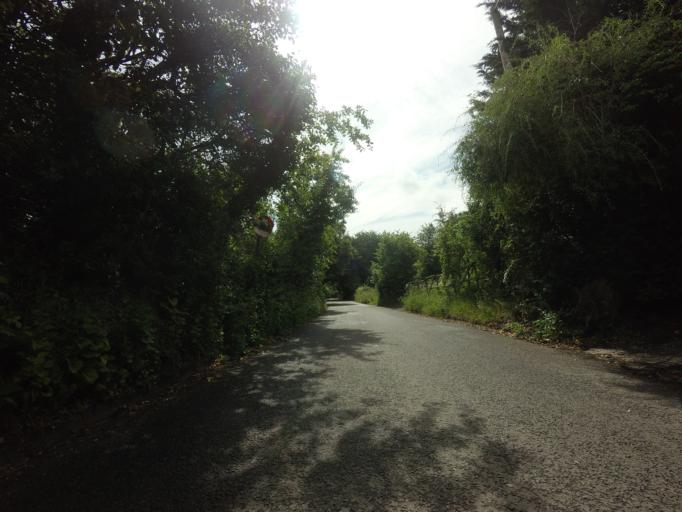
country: GB
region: England
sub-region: Kent
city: Halstead
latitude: 51.3546
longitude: 0.1365
